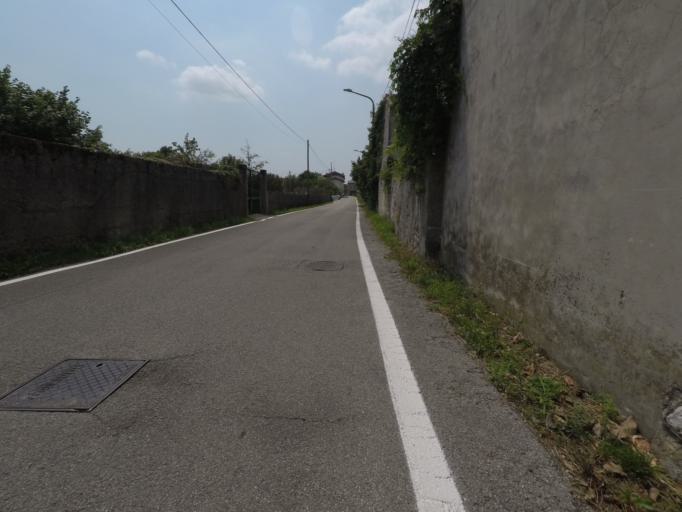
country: IT
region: Friuli Venezia Giulia
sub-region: Provincia di Pordenone
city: Aviano-Castello
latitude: 46.0601
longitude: 12.5776
